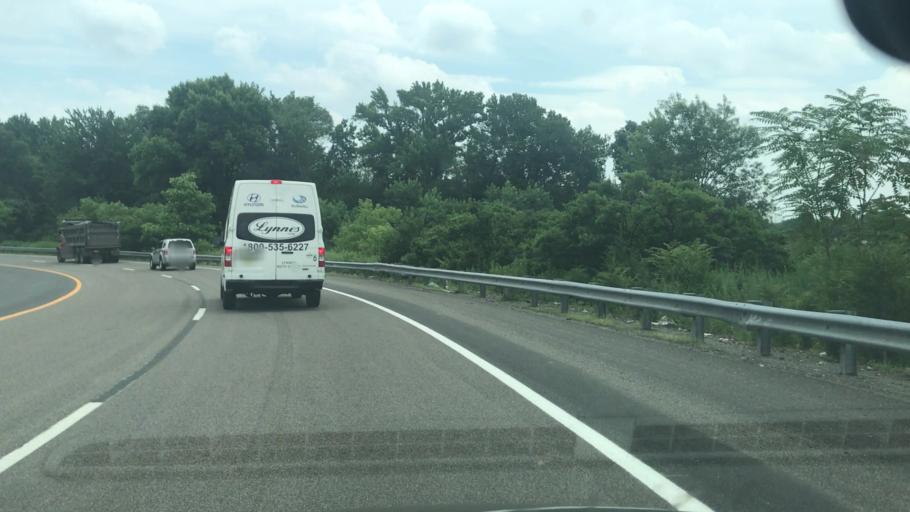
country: US
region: New Jersey
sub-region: Passaic County
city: Singac
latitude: 40.8962
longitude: -74.2517
